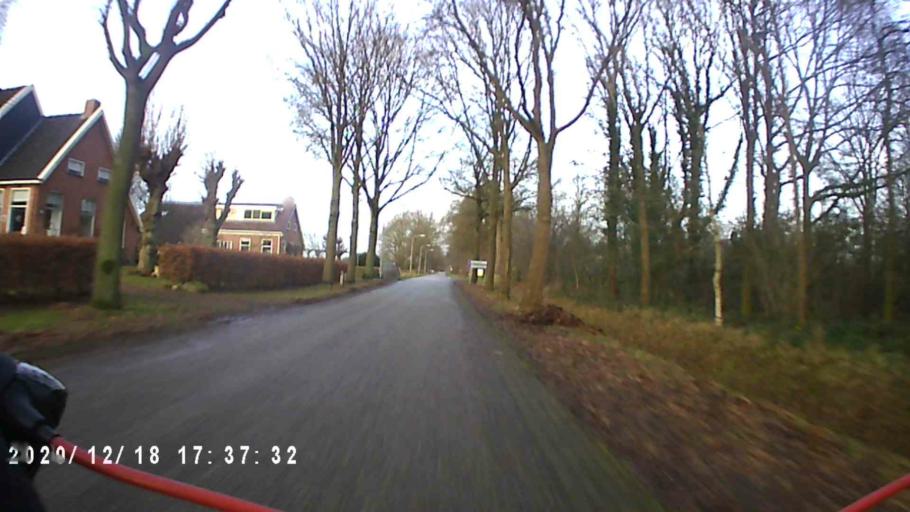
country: NL
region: Drenthe
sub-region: Gemeente Tynaarlo
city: Vries
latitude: 53.0850
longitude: 6.5758
